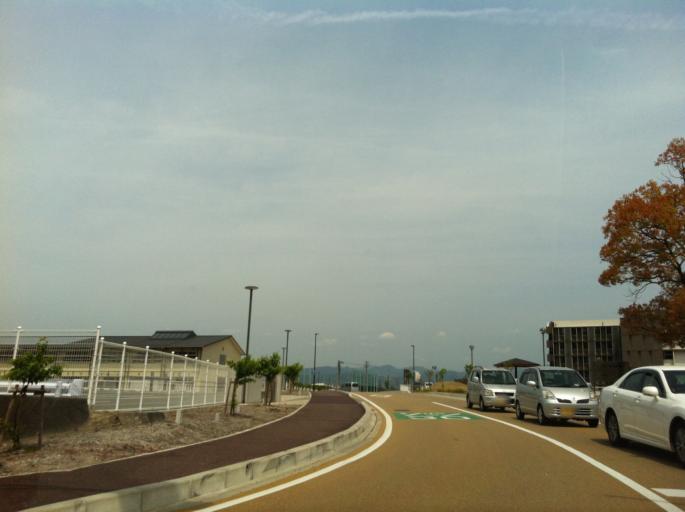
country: JP
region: Shizuoka
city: Kakegawa
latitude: 34.7603
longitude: 138.0264
